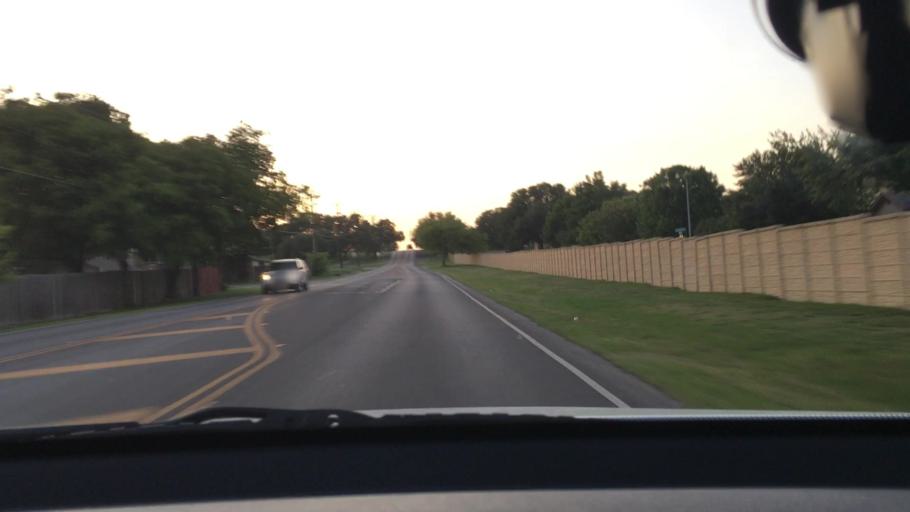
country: US
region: Texas
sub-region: Bexar County
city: Live Oak
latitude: 29.5848
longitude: -98.4052
